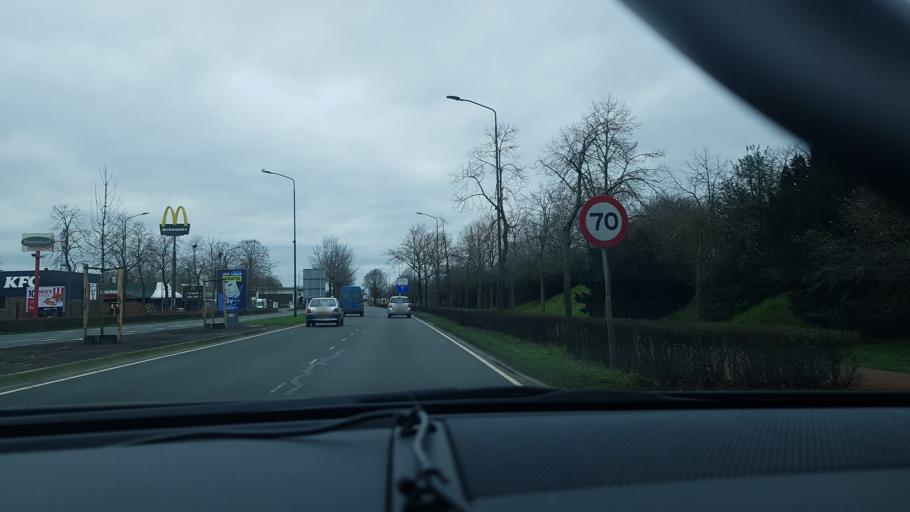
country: NL
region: North Brabant
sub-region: Gemeente Helmond
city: Helmond
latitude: 51.4723
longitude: 5.6995
